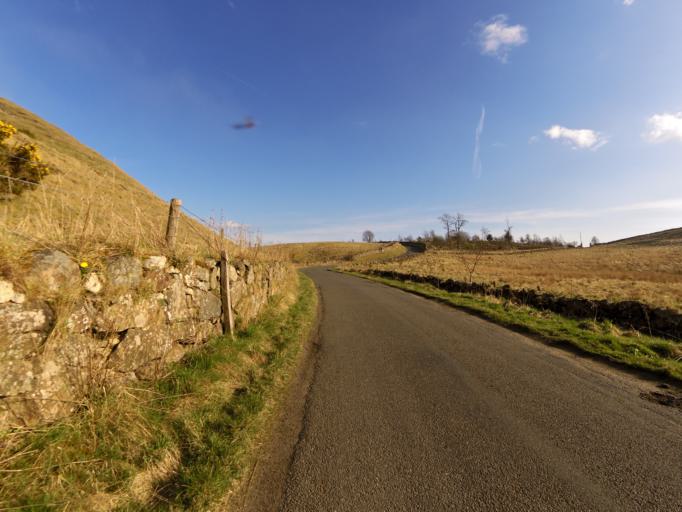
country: GB
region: Scotland
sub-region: Fife
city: Falkland
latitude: 56.2402
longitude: -3.2474
